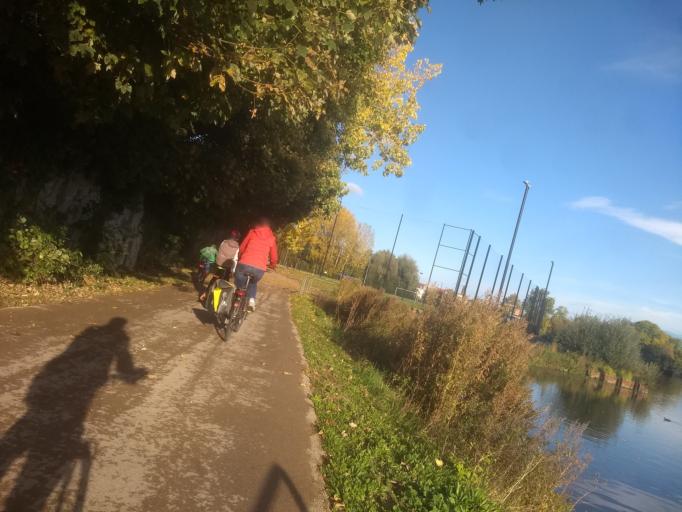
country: FR
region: Nord-Pas-de-Calais
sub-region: Departement du Pas-de-Calais
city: Saint-Laurent-Blangy
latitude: 50.2990
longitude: 2.7947
